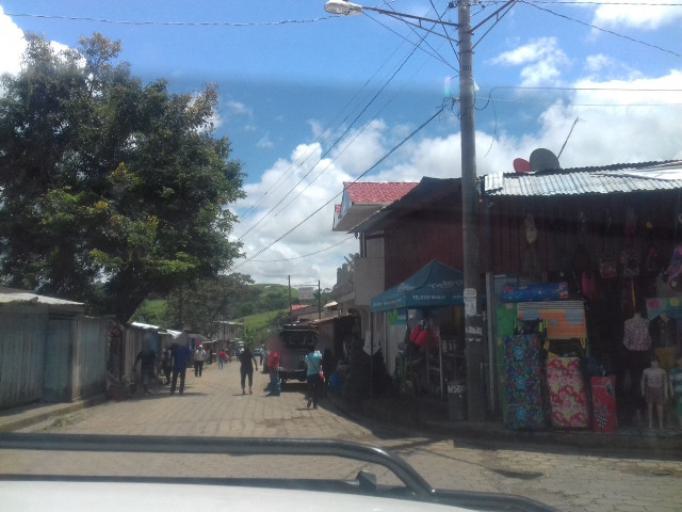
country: NI
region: Atlantico Norte (RAAN)
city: Waslala
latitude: 13.2378
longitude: -85.5588
